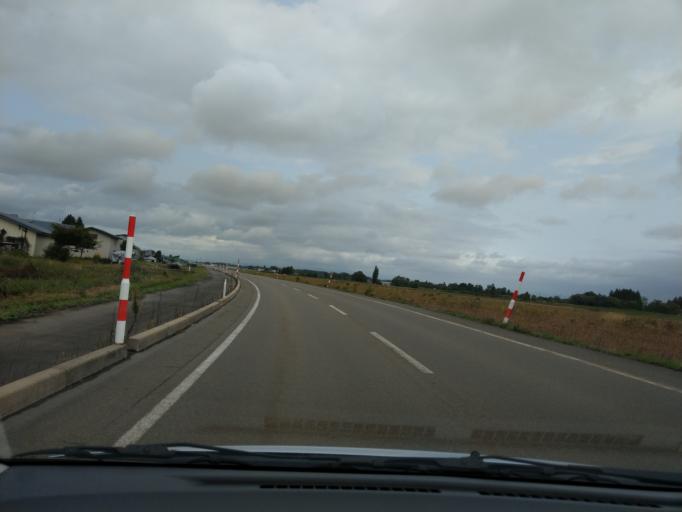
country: JP
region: Akita
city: Omagari
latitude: 39.3831
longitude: 140.4870
